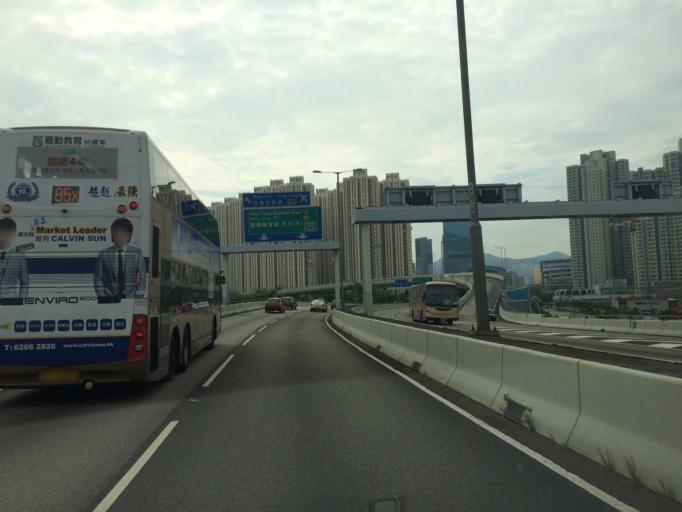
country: HK
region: Wong Tai Sin
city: Wong Tai Sin
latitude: 22.3348
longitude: 114.2049
